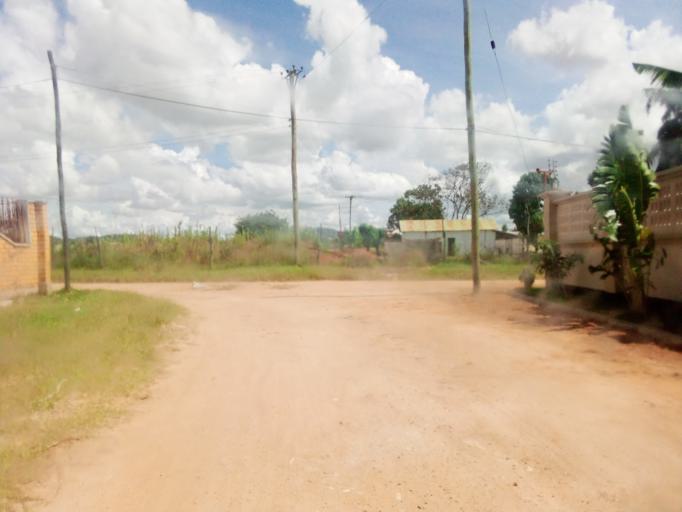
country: TZ
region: Dodoma
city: Dodoma
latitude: -6.1685
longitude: 35.7623
